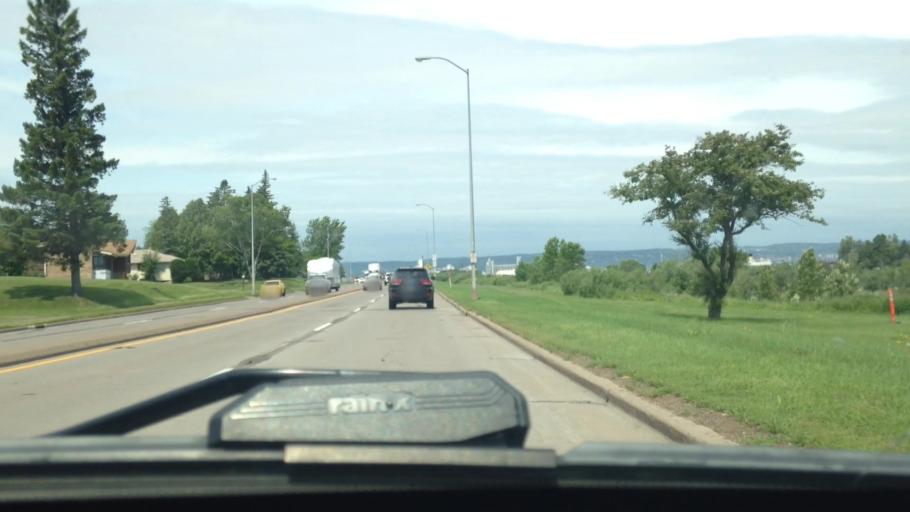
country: US
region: Wisconsin
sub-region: Douglas County
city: Superior
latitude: 46.7155
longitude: -92.0586
